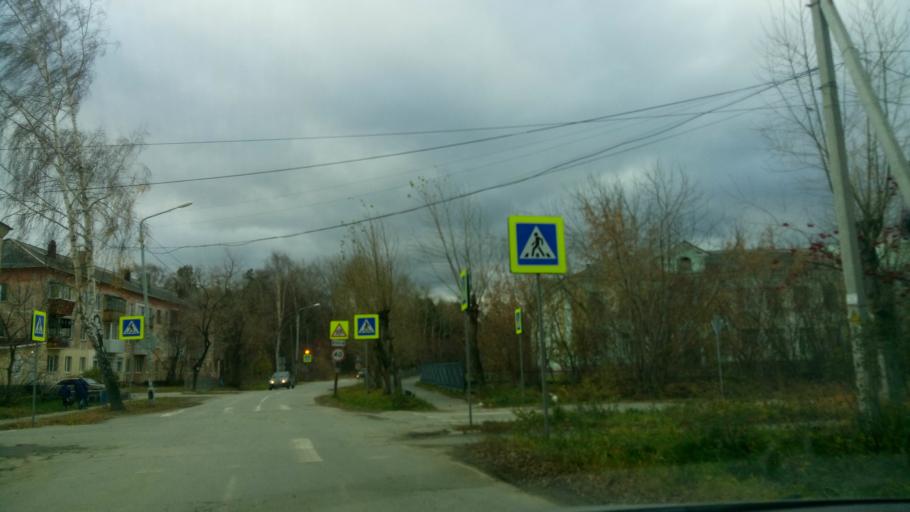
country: RU
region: Sverdlovsk
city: Sredneuralsk
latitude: 56.9903
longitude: 60.4718
